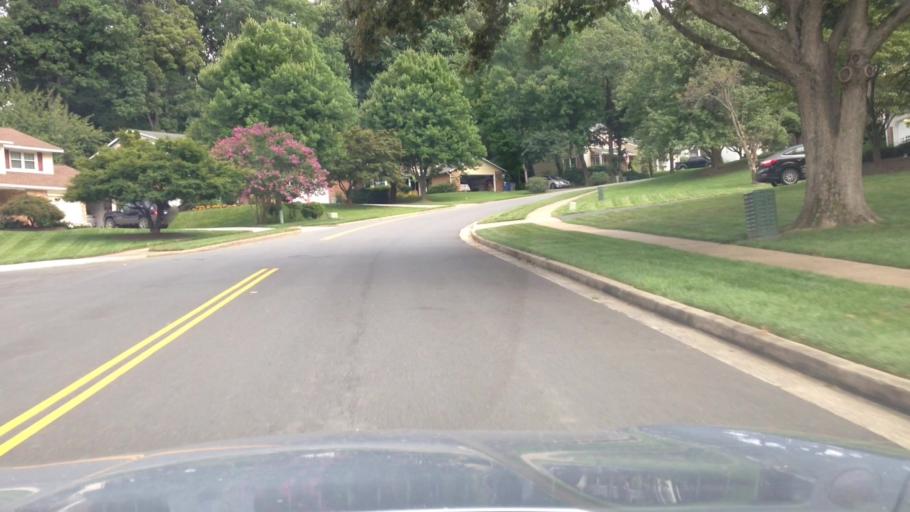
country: US
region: Virginia
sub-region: City of Falls Church
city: Falls Church
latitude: 38.9088
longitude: -77.1647
